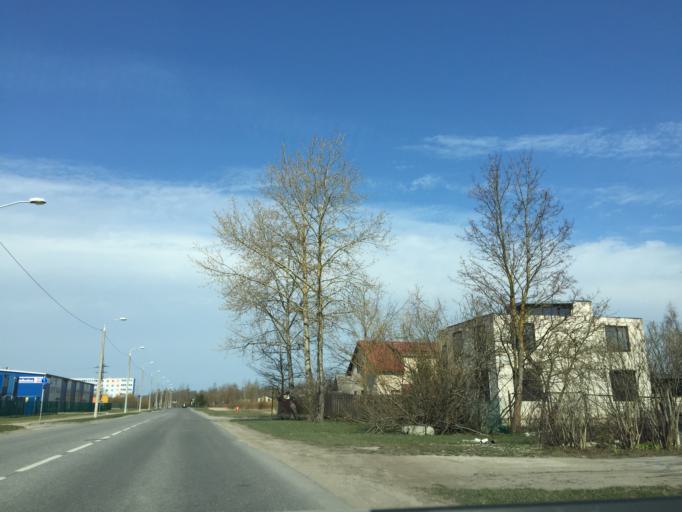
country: EE
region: Ida-Virumaa
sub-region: Narva linn
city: Narva
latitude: 59.3902
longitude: 28.1858
